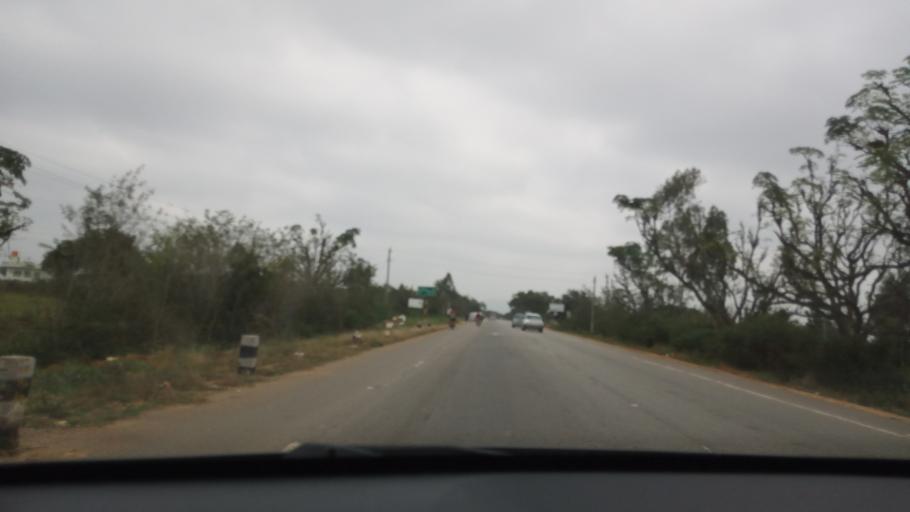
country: IN
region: Karnataka
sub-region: Chikkaballapur
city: Sidlaghatta
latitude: 13.2807
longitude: 77.9564
